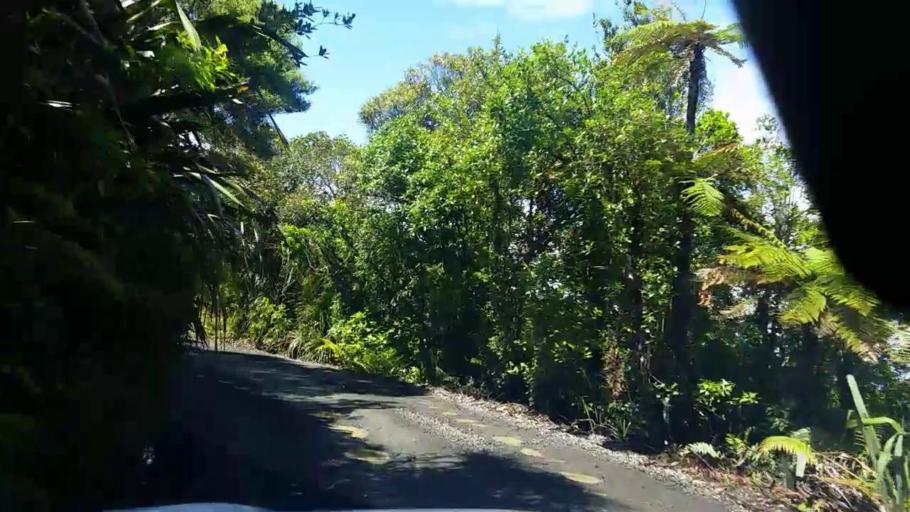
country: NZ
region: Auckland
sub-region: Auckland
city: Titirangi
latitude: -36.9410
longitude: 174.5190
